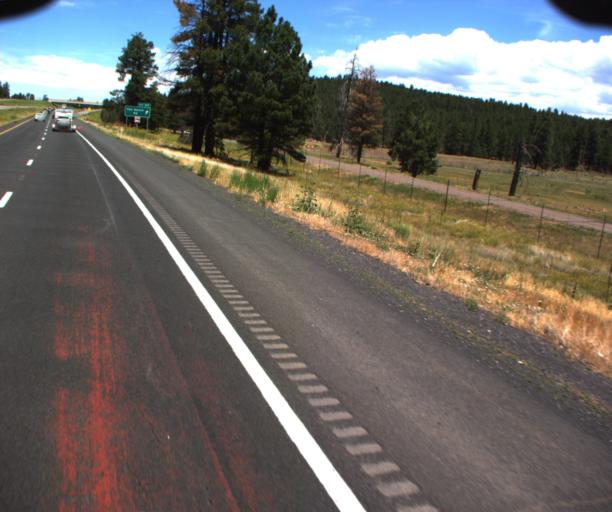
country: US
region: Arizona
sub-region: Coconino County
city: Sedona
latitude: 34.8698
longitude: -111.6299
